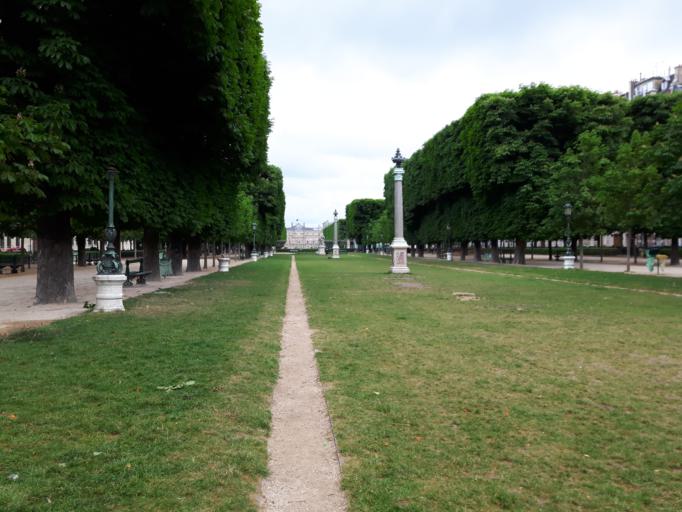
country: FR
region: Ile-de-France
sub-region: Paris
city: Paris
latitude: 48.8429
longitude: 2.3368
